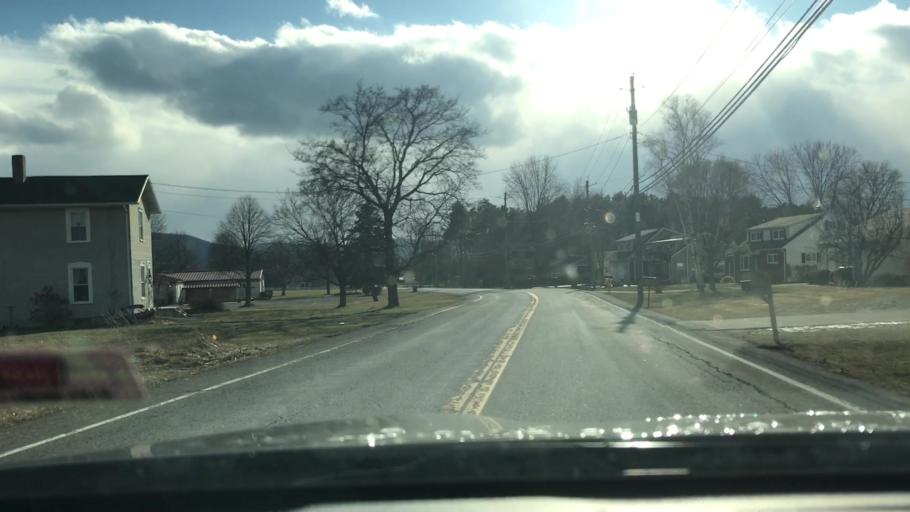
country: US
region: New York
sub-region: Chemung County
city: Big Flats
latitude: 42.1546
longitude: -76.9249
